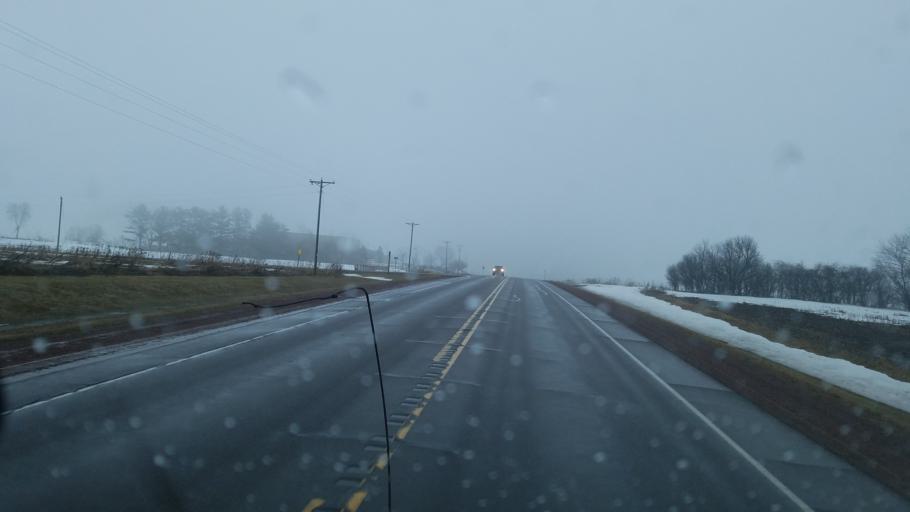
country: US
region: Wisconsin
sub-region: Wood County
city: Marshfield
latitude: 44.5988
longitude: -90.2695
